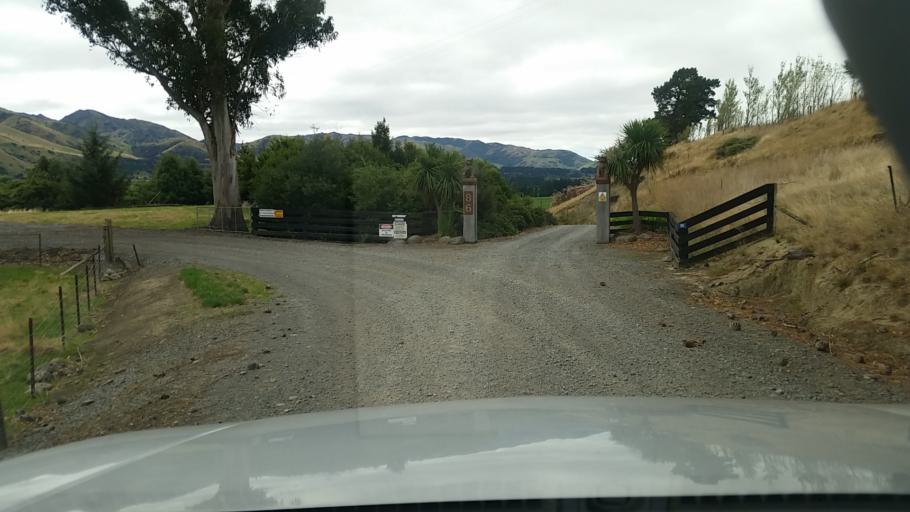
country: NZ
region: Marlborough
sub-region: Marlborough District
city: Blenheim
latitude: -41.6949
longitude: 173.9485
